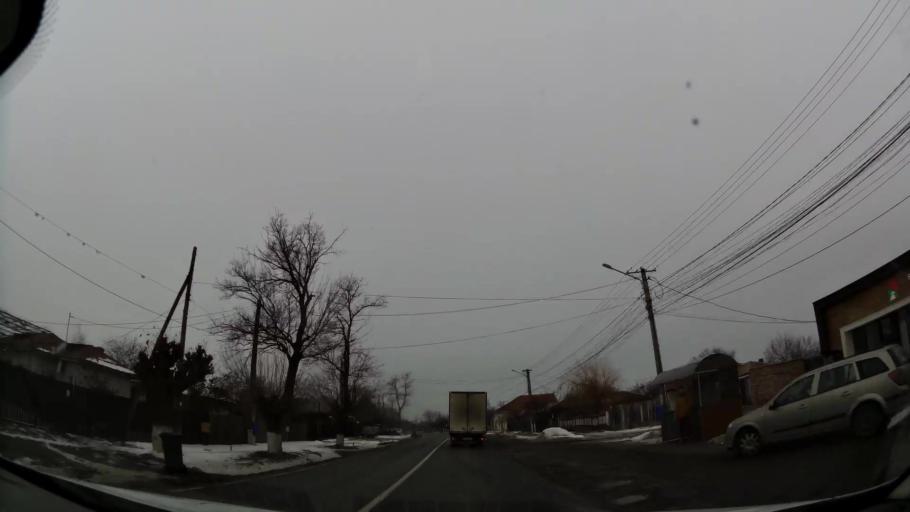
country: RO
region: Dambovita
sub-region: Comuna Tartasesti
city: Baldana
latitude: 44.6147
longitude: 25.7643
